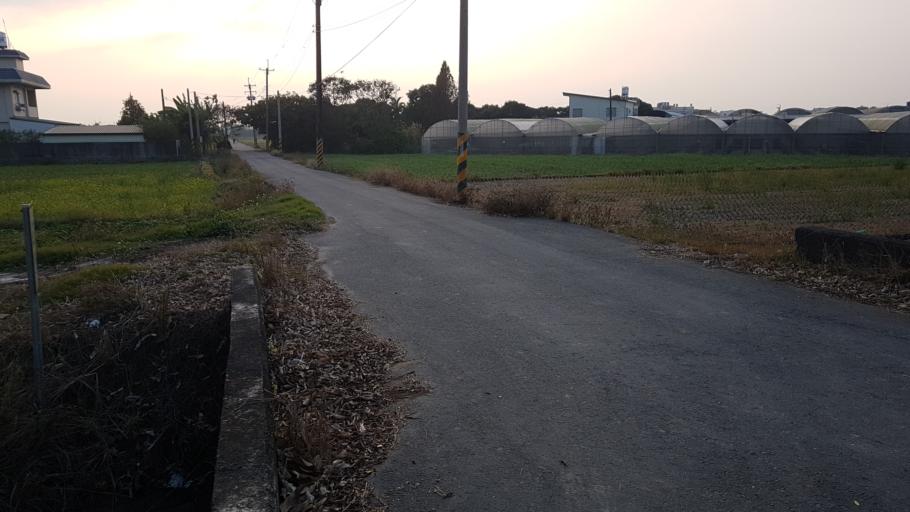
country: TW
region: Taiwan
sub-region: Chiayi
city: Jiayi Shi
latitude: 23.3763
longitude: 120.4531
